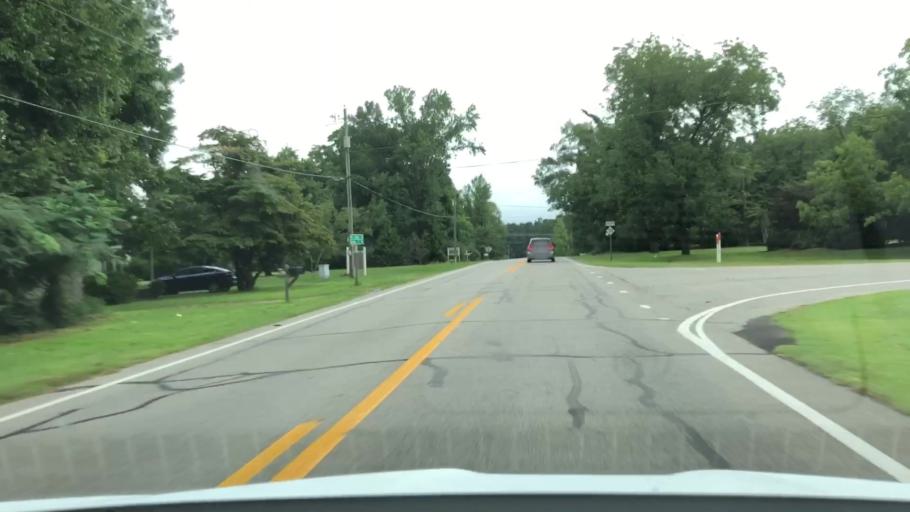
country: US
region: North Carolina
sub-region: Lenoir County
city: Kinston
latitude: 35.2149
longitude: -77.5702
